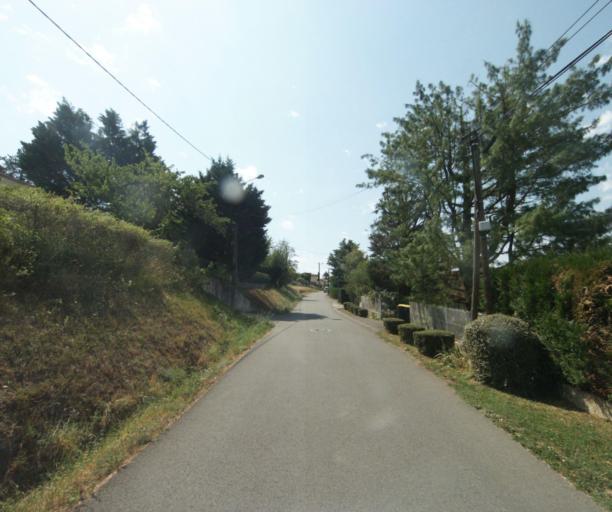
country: FR
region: Rhone-Alpes
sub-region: Departement du Rhone
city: Lentilly
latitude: 45.8358
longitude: 4.6398
